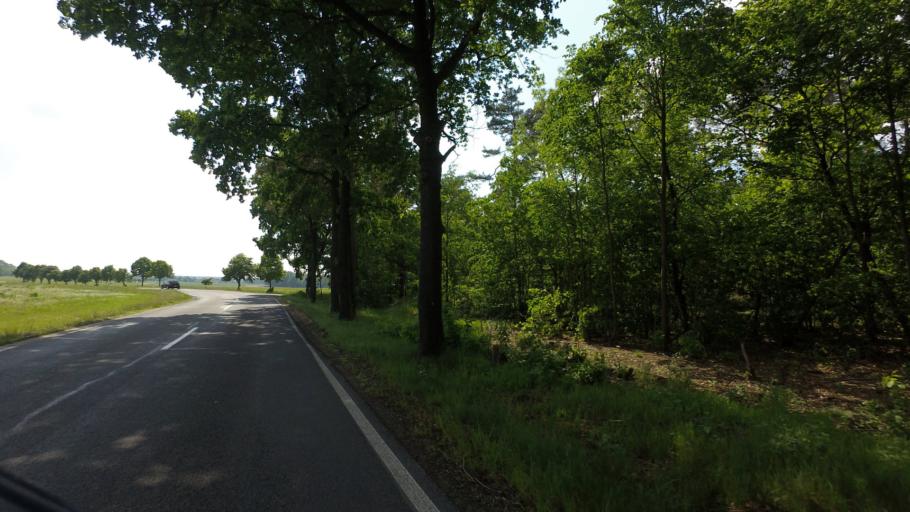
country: DE
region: Saxony
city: Mucka
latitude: 51.2804
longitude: 14.6545
